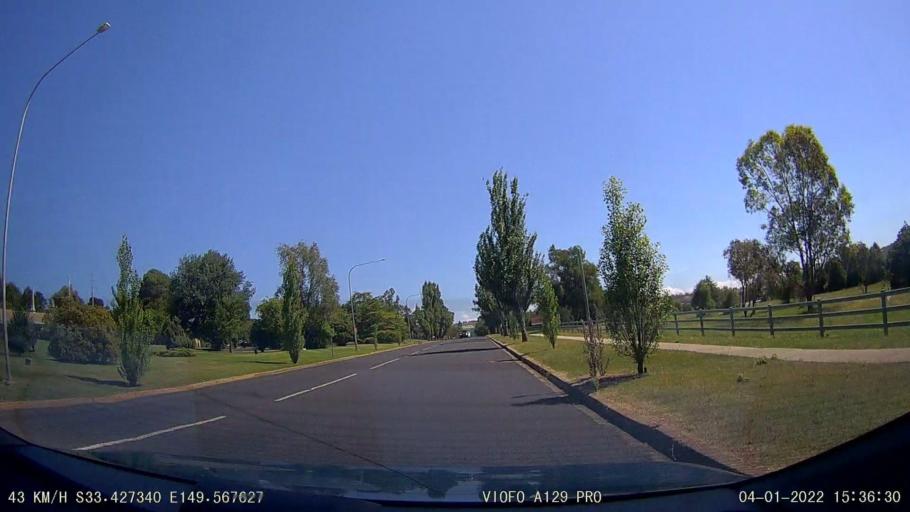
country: AU
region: New South Wales
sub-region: Bathurst Regional
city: Bathurst
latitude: -33.4271
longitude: 149.5678
